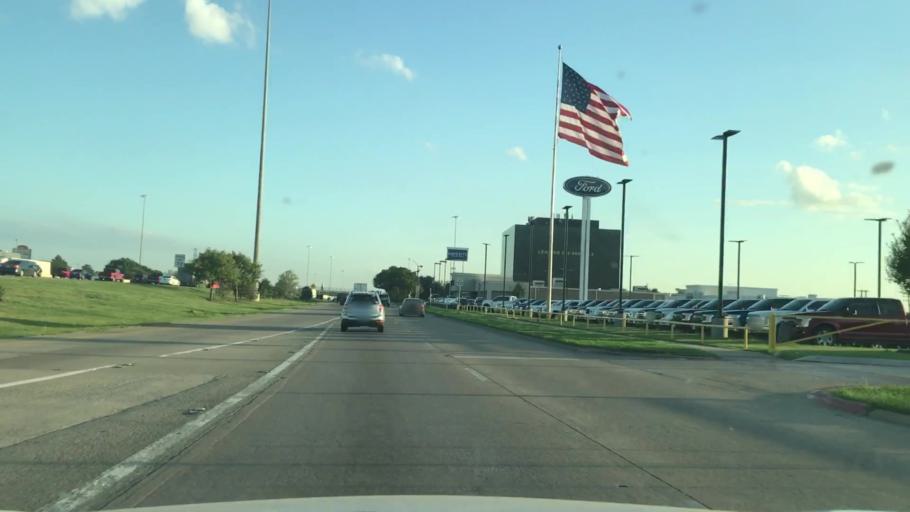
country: US
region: Texas
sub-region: Dallas County
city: Mesquite
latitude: 32.8063
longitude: -96.6278
